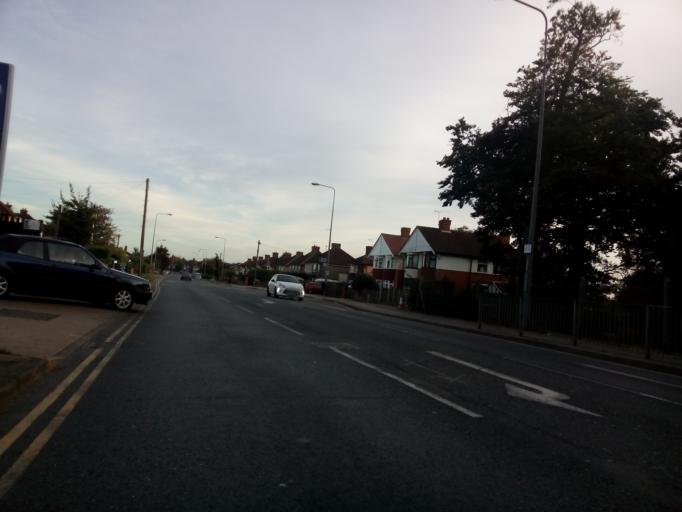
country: GB
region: England
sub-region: Suffolk
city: Bramford
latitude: 52.0784
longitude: 1.1262
